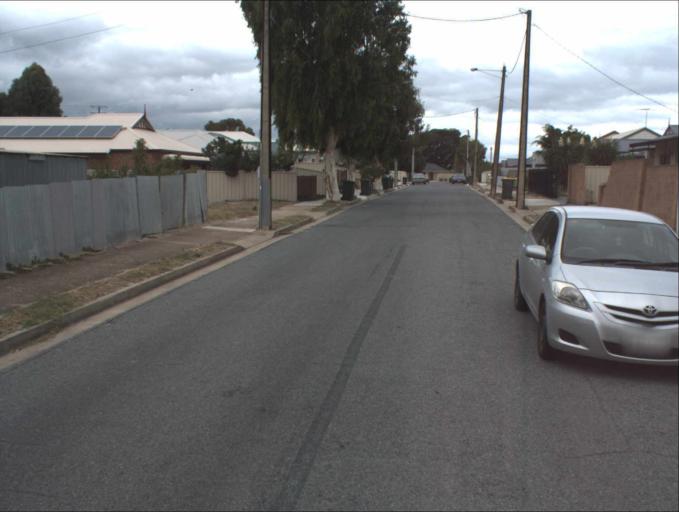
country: AU
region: South Australia
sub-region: Port Adelaide Enfield
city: Birkenhead
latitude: -34.8012
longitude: 138.4978
